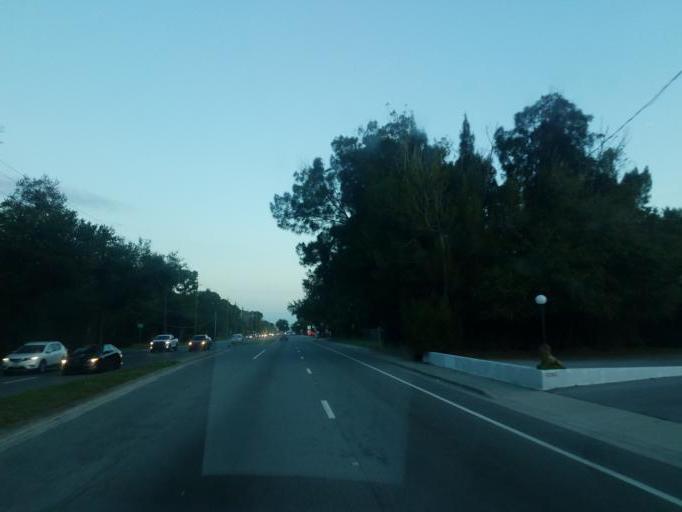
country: US
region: Florida
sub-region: Sarasota County
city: North Sarasota
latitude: 27.3791
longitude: -82.5056
